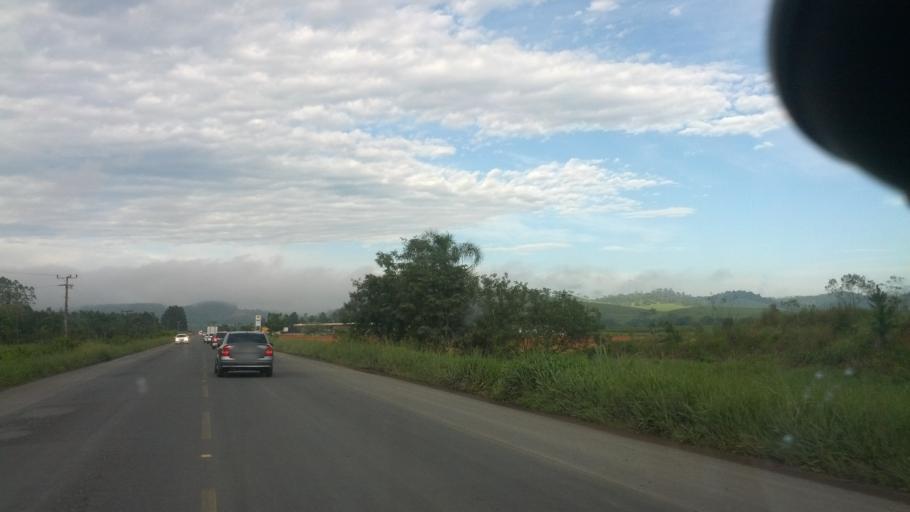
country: BR
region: Santa Catarina
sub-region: Otacilio Costa
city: Otacilio Costa
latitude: -27.2485
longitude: -49.9830
